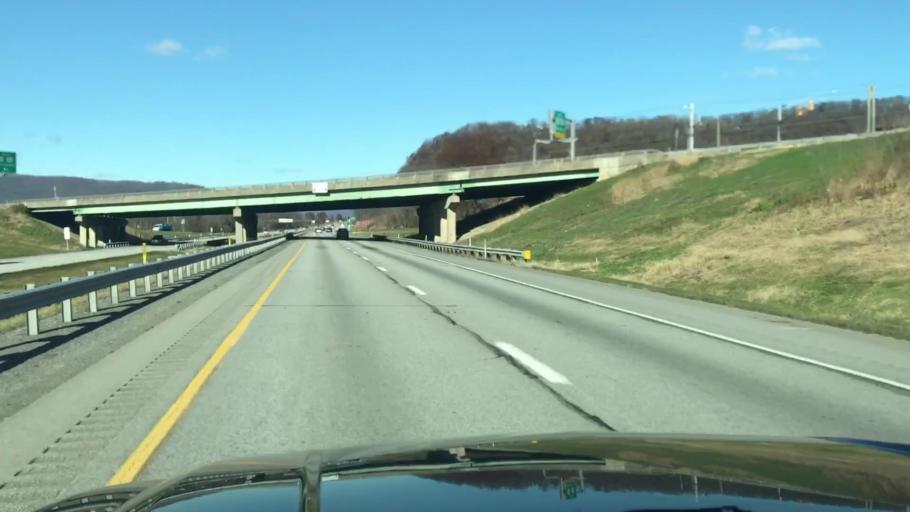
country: US
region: Pennsylvania
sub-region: Perry County
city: Marysville
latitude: 40.3253
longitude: -76.8897
